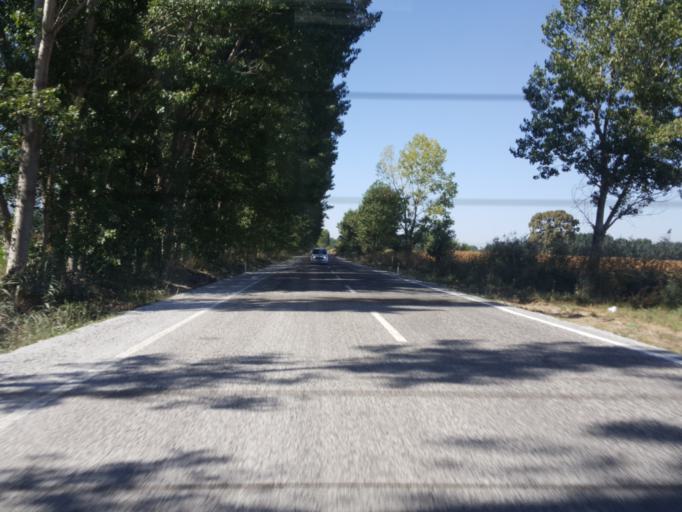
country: TR
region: Tokat
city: Pazar
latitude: 40.2694
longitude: 36.2244
